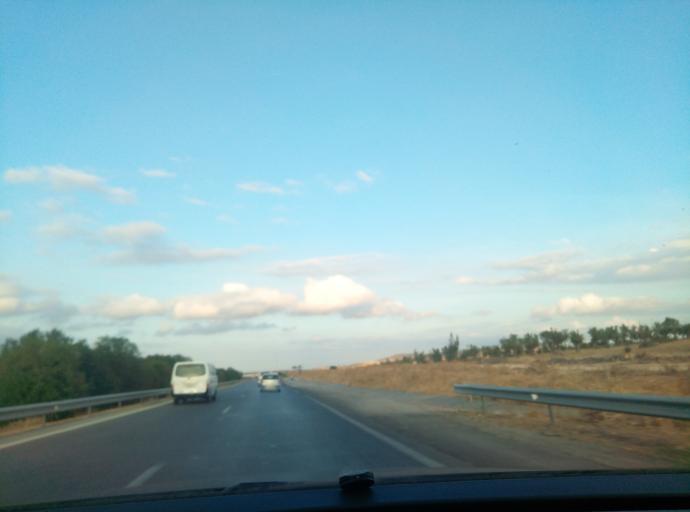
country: TN
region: Manouba
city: El Battan
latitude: 36.6660
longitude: 9.8673
